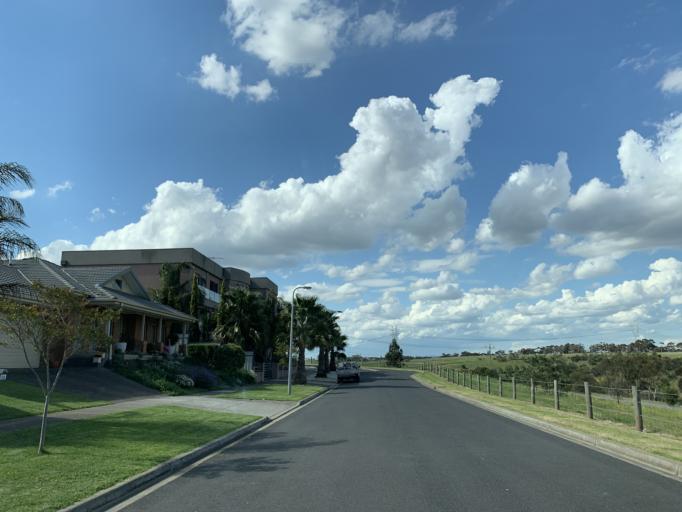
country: AU
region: Victoria
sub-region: Brimbank
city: Kealba
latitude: -37.7375
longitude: 144.8324
